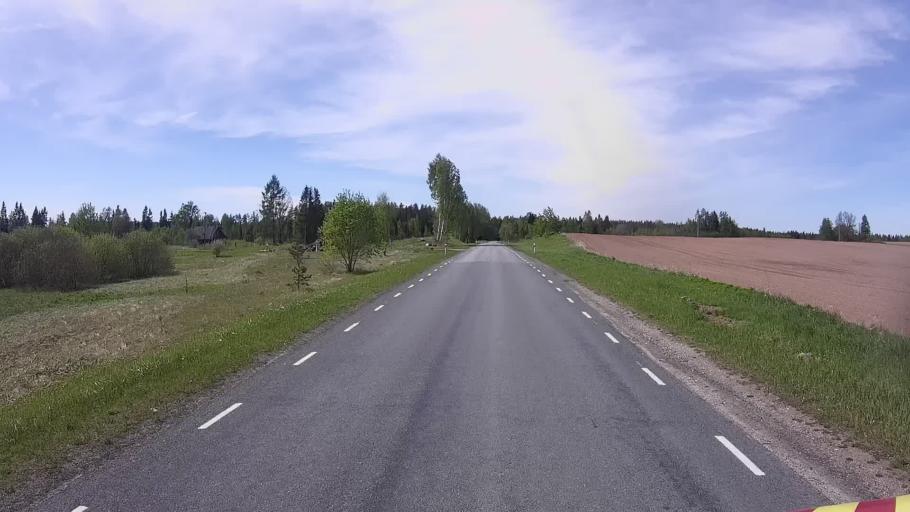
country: EE
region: Valgamaa
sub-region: Valga linn
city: Valga
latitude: 57.6948
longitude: 26.2631
